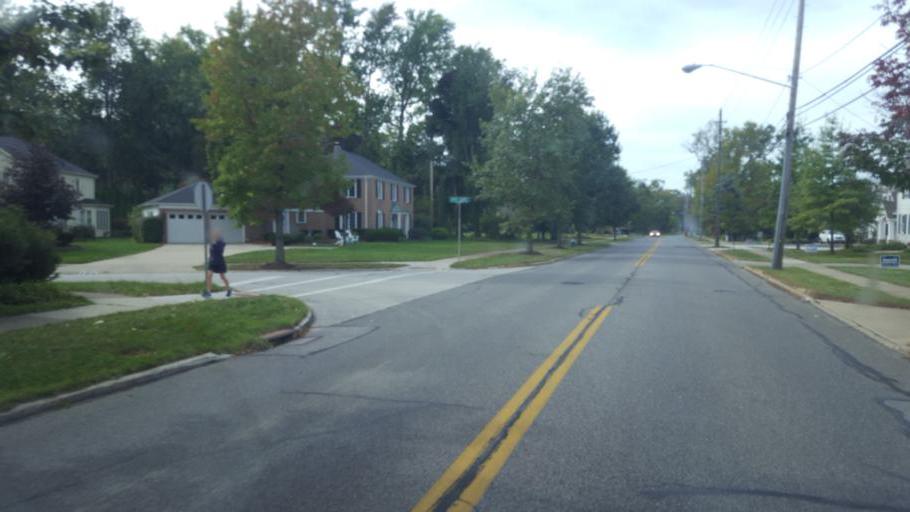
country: US
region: Ohio
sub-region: Cuyahoga County
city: Bay Village
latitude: 41.4921
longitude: -81.9455
